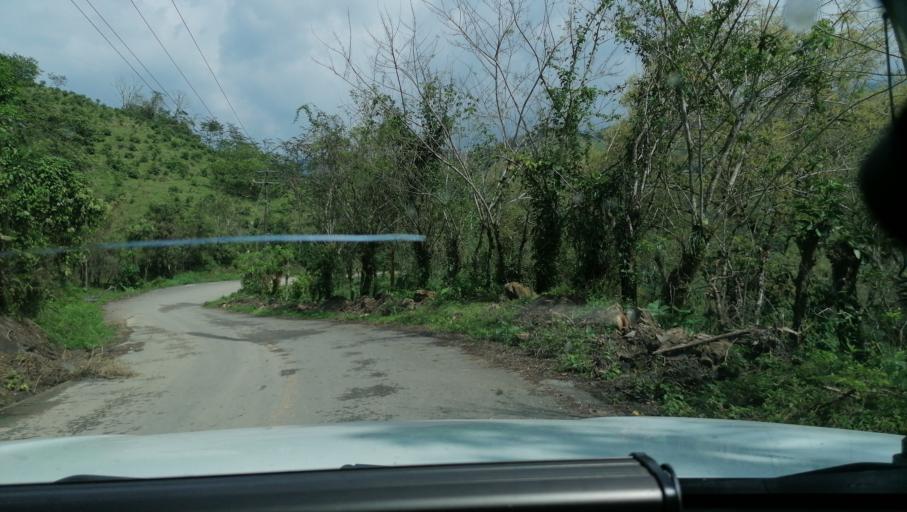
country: MX
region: Chiapas
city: Ocotepec
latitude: 17.3111
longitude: -93.1763
